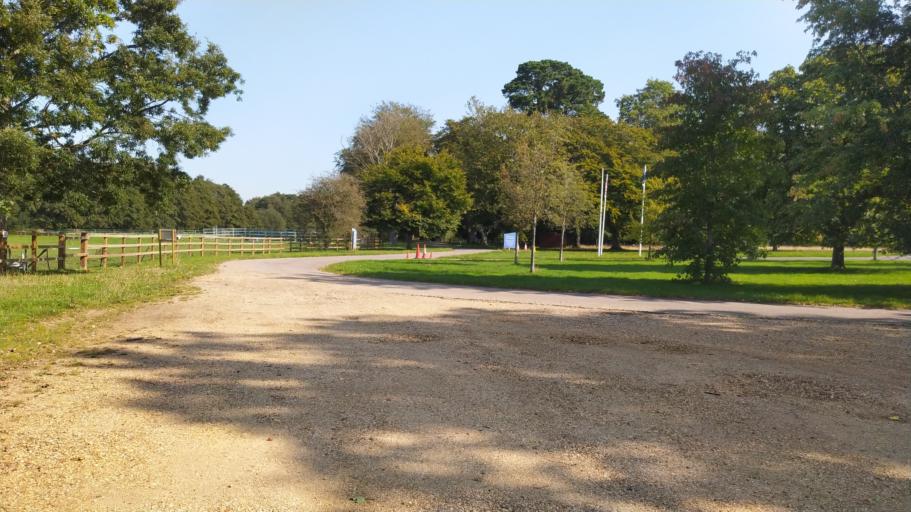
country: GB
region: England
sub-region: Hampshire
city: Lyndhurst
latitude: 50.8625
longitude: -1.5771
